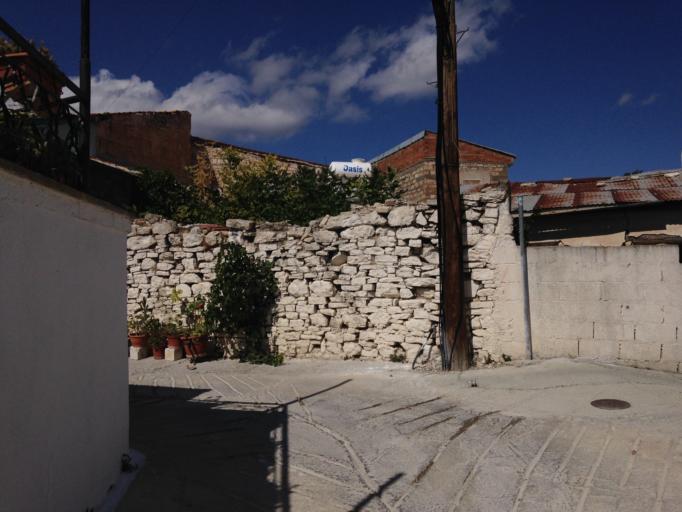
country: CY
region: Limassol
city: Pachna
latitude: 34.8481
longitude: 32.8101
